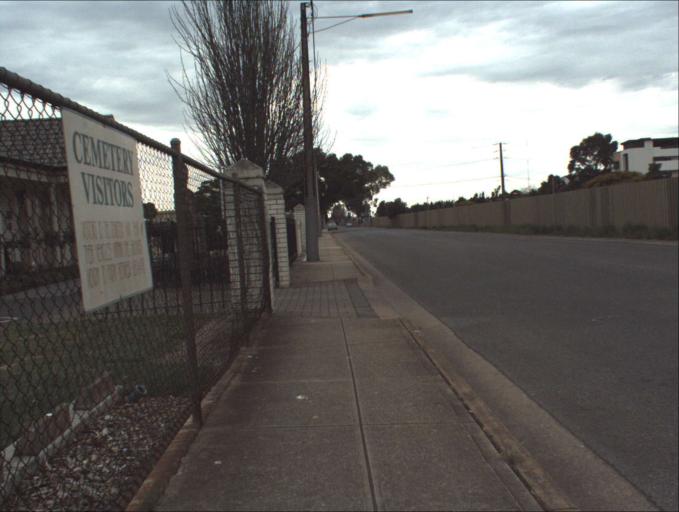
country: AU
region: South Australia
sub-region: Prospect
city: Prospect
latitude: -34.8839
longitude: 138.5829
